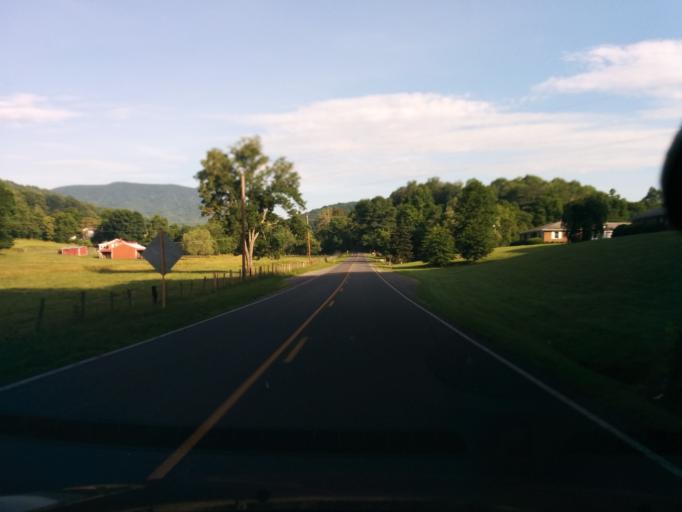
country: US
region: Virginia
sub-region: City of Lexington
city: Lexington
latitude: 37.8156
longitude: -79.4847
